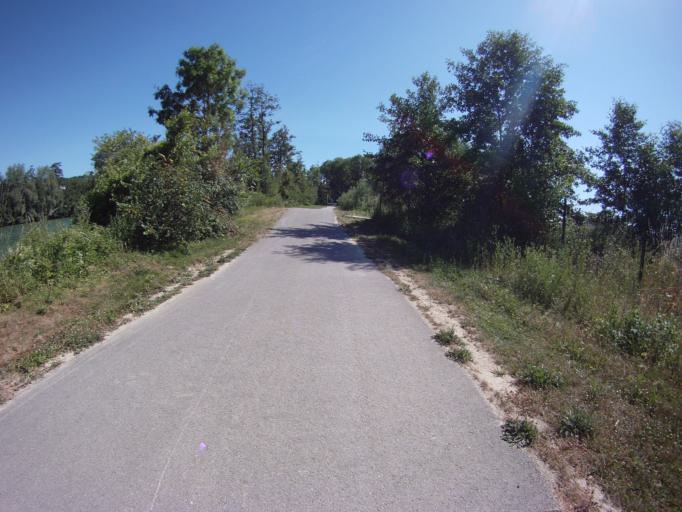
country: FR
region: Champagne-Ardenne
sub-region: Departement de la Marne
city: Dormans
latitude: 49.0810
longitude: 3.6387
